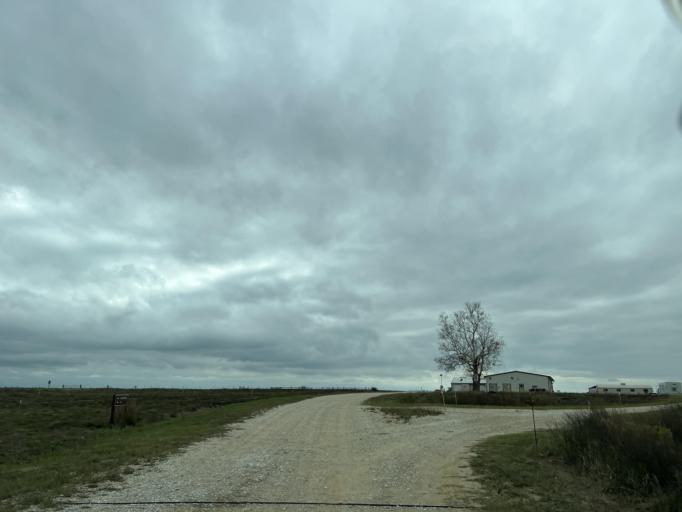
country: US
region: Texas
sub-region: Colorado County
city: Eagle Lake
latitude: 29.6688
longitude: -96.2657
